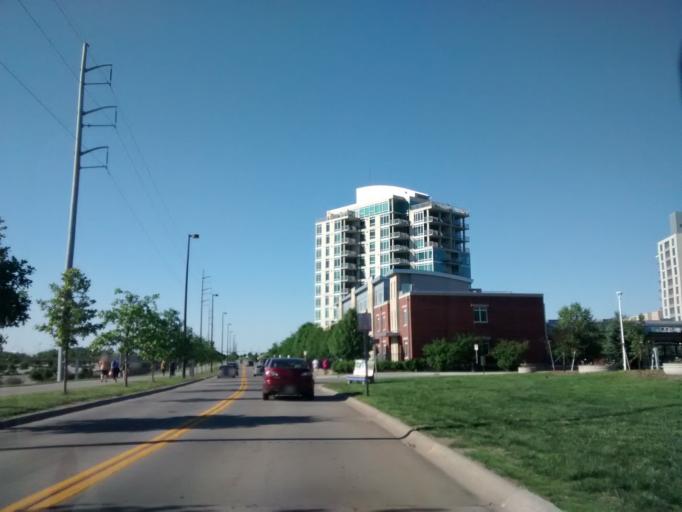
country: US
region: Nebraska
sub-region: Douglas County
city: Omaha
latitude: 41.2657
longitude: -95.9256
